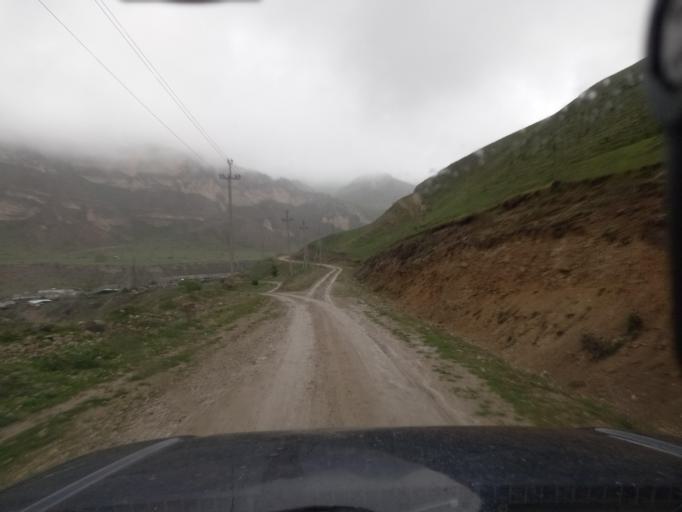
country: RU
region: Kabardino-Balkariya
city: Zhankhoteko
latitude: 43.5064
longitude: 43.1557
